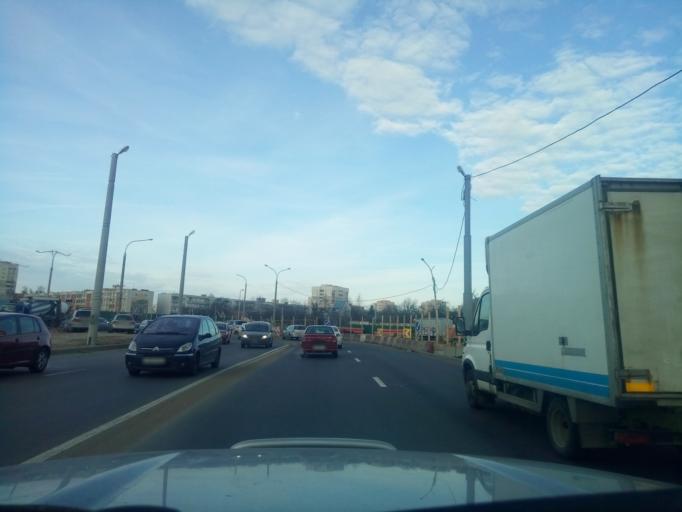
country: BY
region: Minsk
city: Minsk
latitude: 53.8722
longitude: 27.5459
